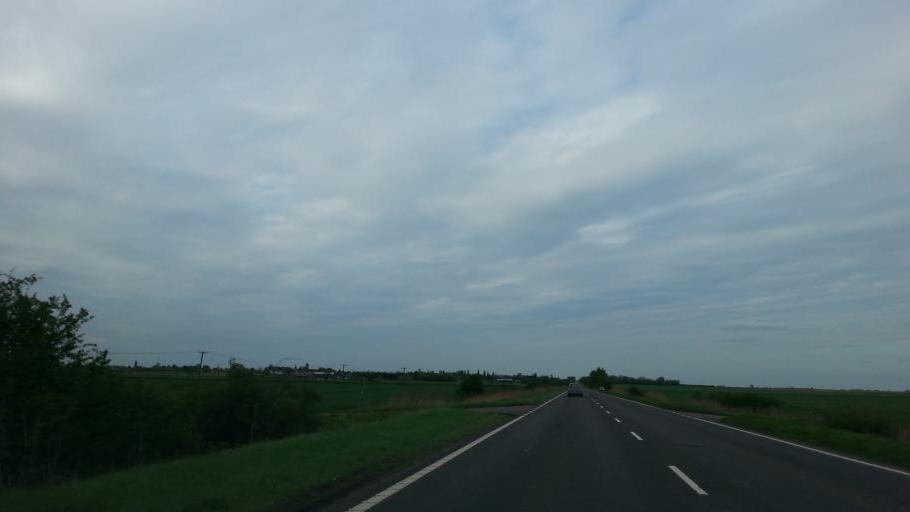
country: GB
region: England
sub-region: Cambridgeshire
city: Doddington
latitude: 52.4770
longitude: 0.0549
